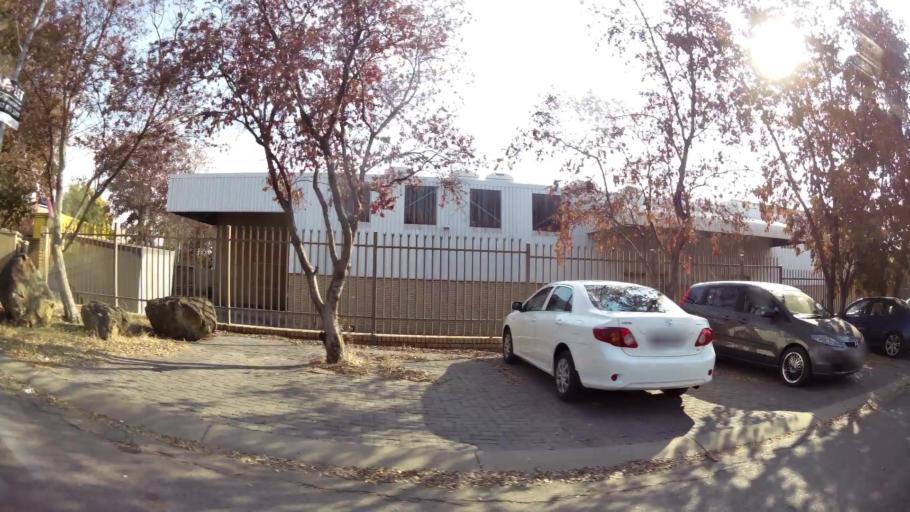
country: ZA
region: Gauteng
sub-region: City of Johannesburg Metropolitan Municipality
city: Modderfontein
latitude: -26.1062
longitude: 28.1761
